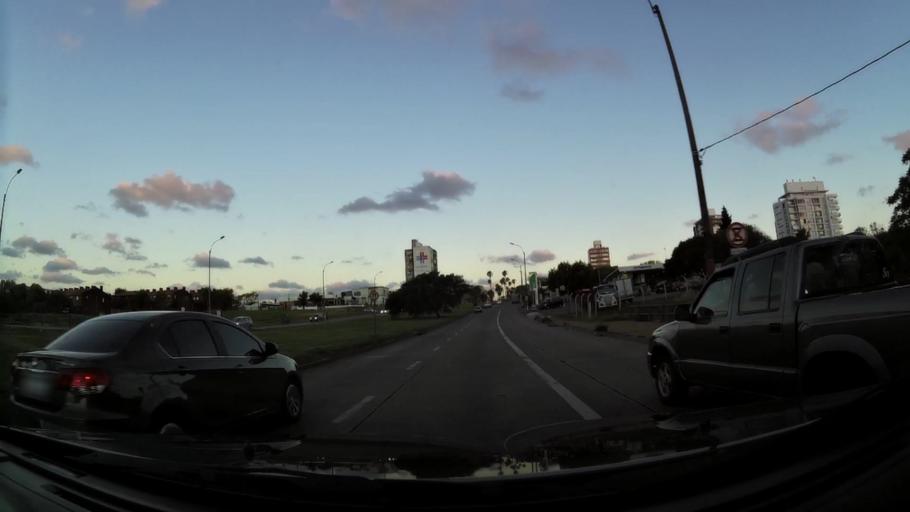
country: UY
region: Canelones
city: Paso de Carrasco
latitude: -34.8862
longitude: -56.1054
